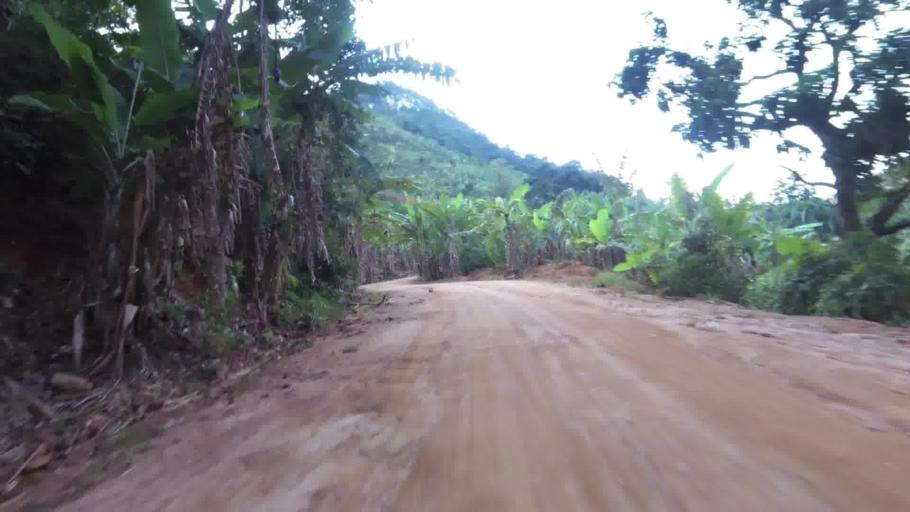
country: BR
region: Espirito Santo
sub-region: Alfredo Chaves
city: Alfredo Chaves
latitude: -20.5625
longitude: -40.6932
